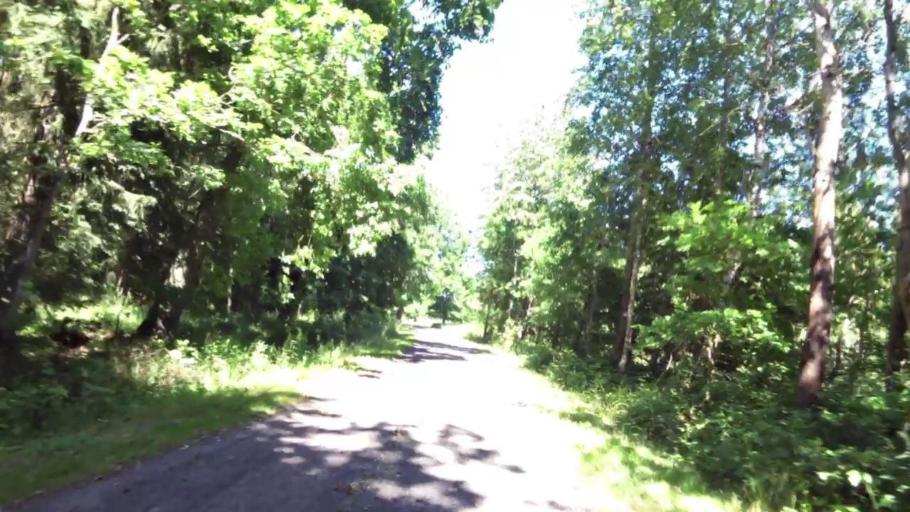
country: PL
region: West Pomeranian Voivodeship
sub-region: Powiat kolobrzeski
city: Goscino
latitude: 54.0413
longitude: 15.7217
